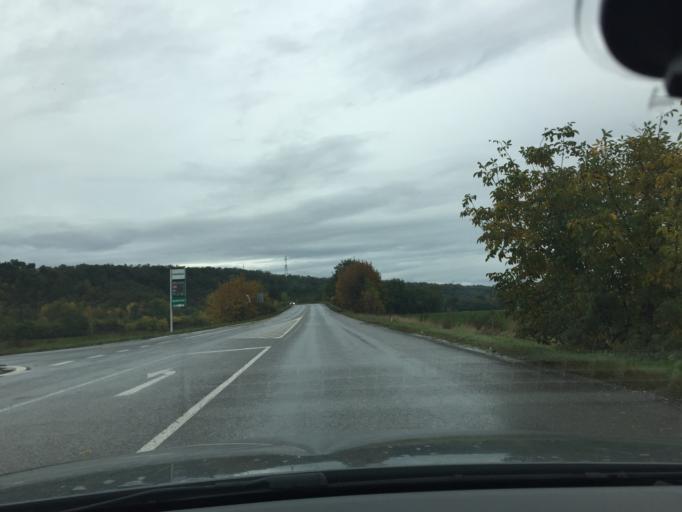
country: CZ
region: Central Bohemia
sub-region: Okres Melnik
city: Veltrusy
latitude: 50.2865
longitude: 14.3128
